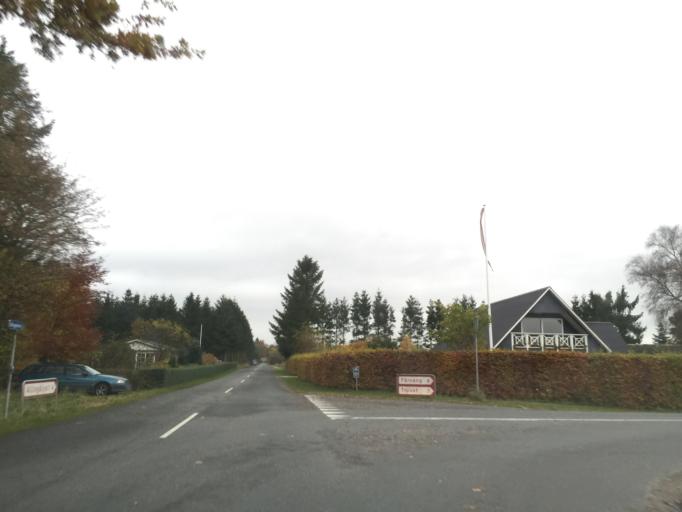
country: DK
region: Central Jutland
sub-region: Silkeborg Kommune
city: Svejbaek
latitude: 56.2392
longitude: 9.6631
